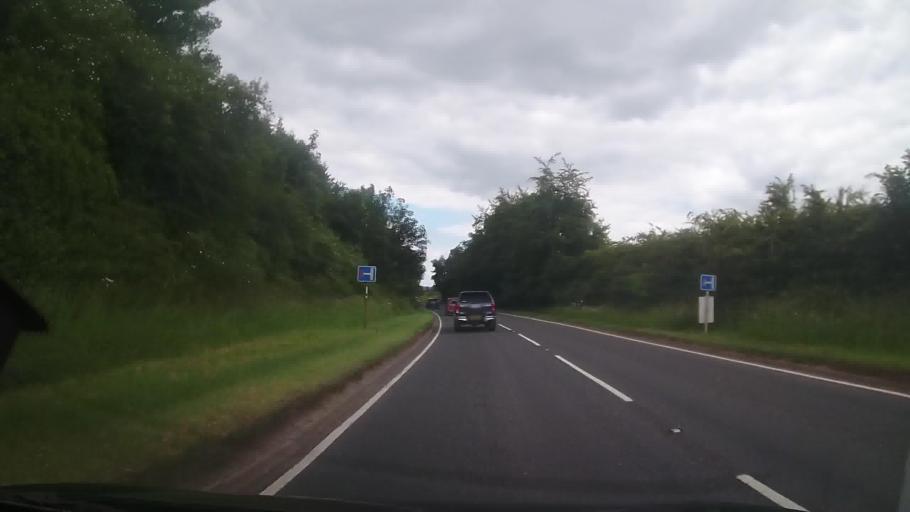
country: GB
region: England
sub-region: Herefordshire
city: Wellington
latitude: 52.1011
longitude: -2.7285
